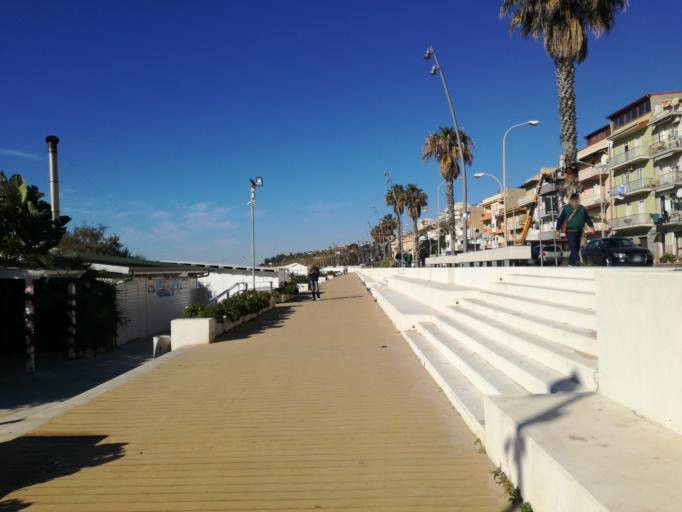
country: IT
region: Sicily
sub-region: Provincia di Caltanissetta
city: Gela
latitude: 37.0651
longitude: 14.2454
